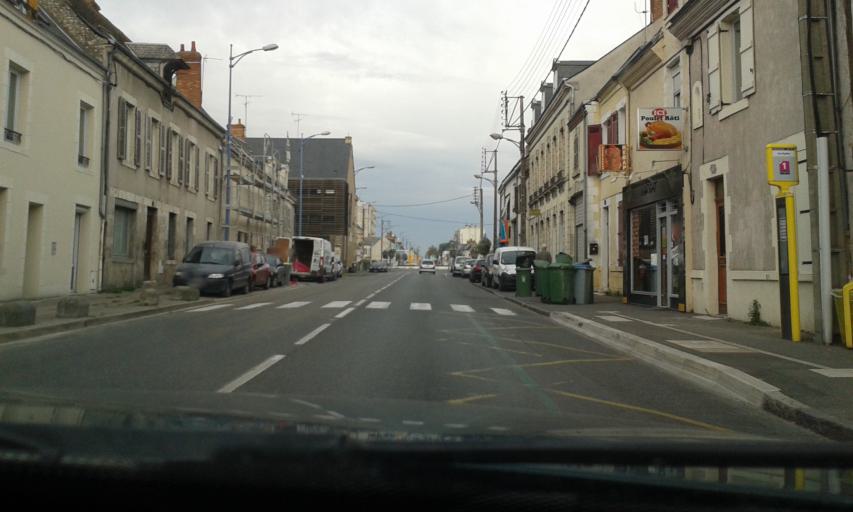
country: FR
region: Centre
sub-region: Departement du Loiret
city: Fleury-les-Aubrais
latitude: 47.9329
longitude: 1.8950
